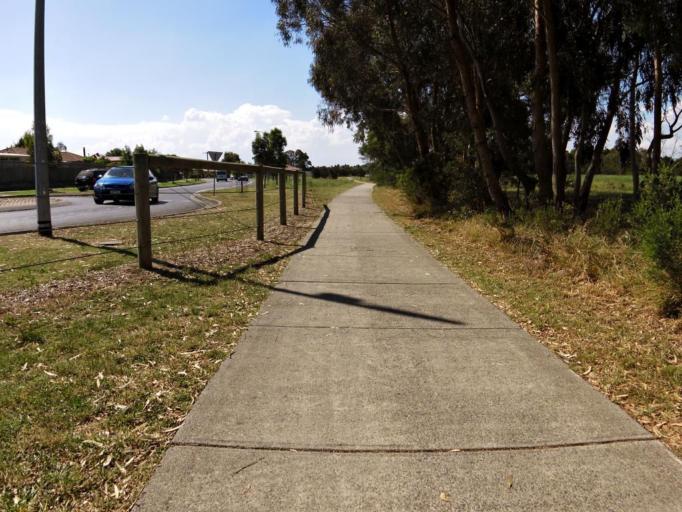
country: AU
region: Victoria
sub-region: Casey
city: Narre Warren South
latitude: -38.0397
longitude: 145.2744
